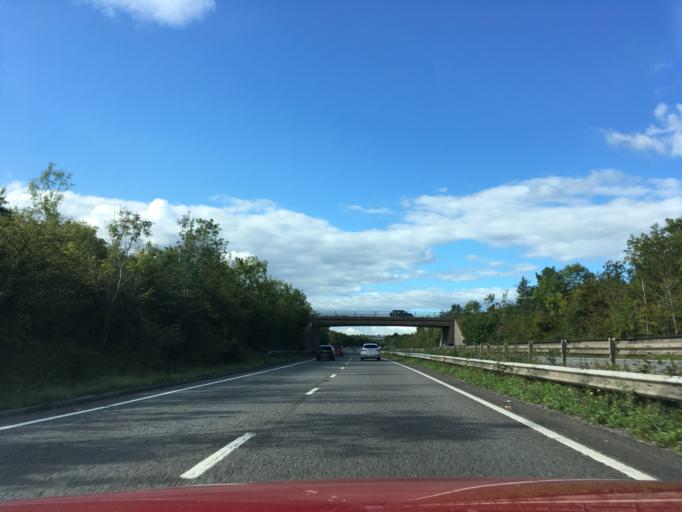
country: GB
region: England
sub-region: Devon
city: Chudleigh
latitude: 50.5944
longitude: -3.6140
